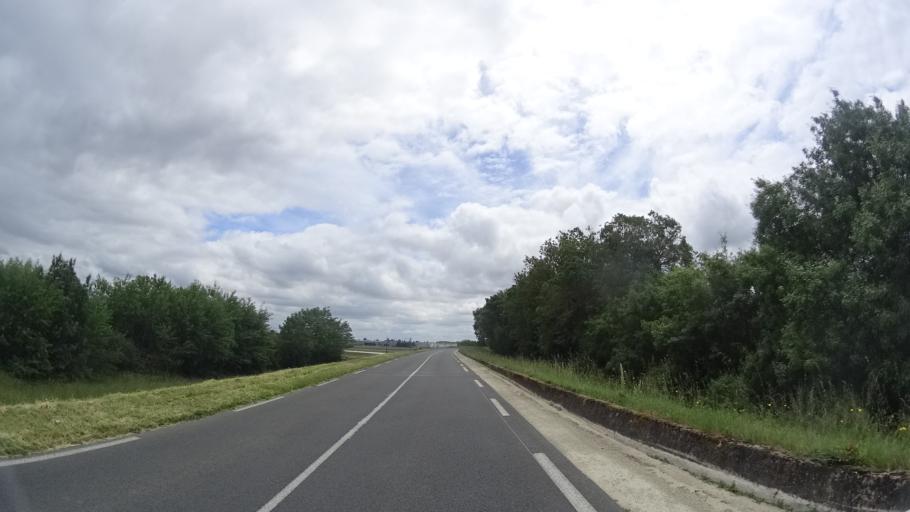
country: FR
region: Pays de la Loire
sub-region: Departement de Maine-et-Loire
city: La Menitre
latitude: 47.4051
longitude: -0.2894
